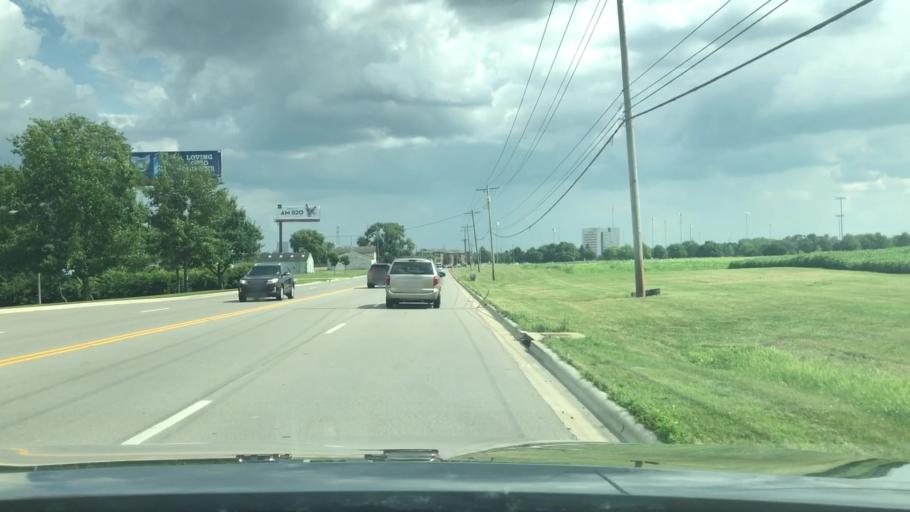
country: US
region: Ohio
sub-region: Franklin County
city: Upper Arlington
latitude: 40.0110
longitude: -83.0363
